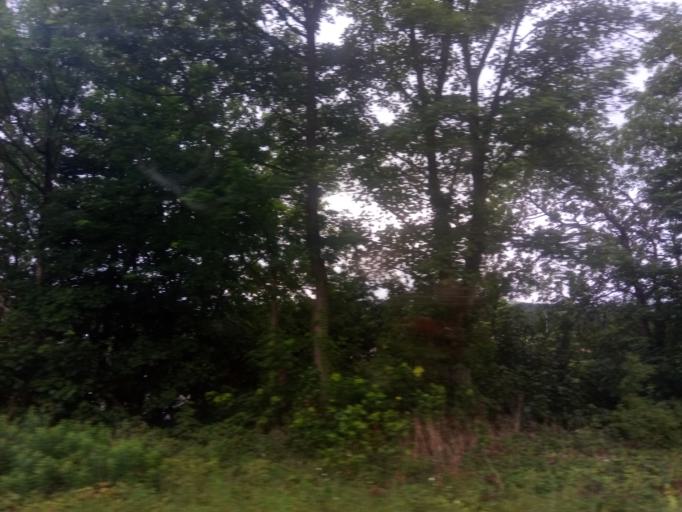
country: GB
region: England
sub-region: North Yorkshire
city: Settle
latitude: 54.0654
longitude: -2.2818
